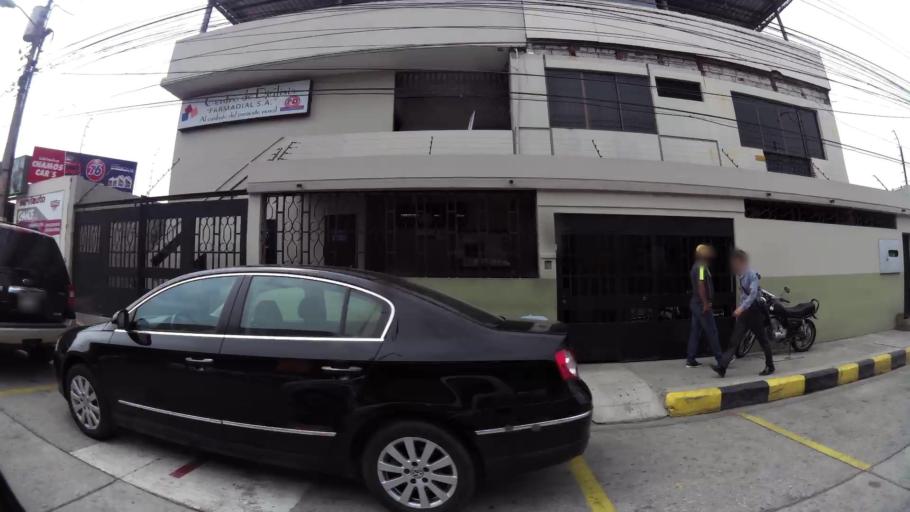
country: EC
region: Guayas
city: Eloy Alfaro
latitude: -2.1475
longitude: -79.8991
